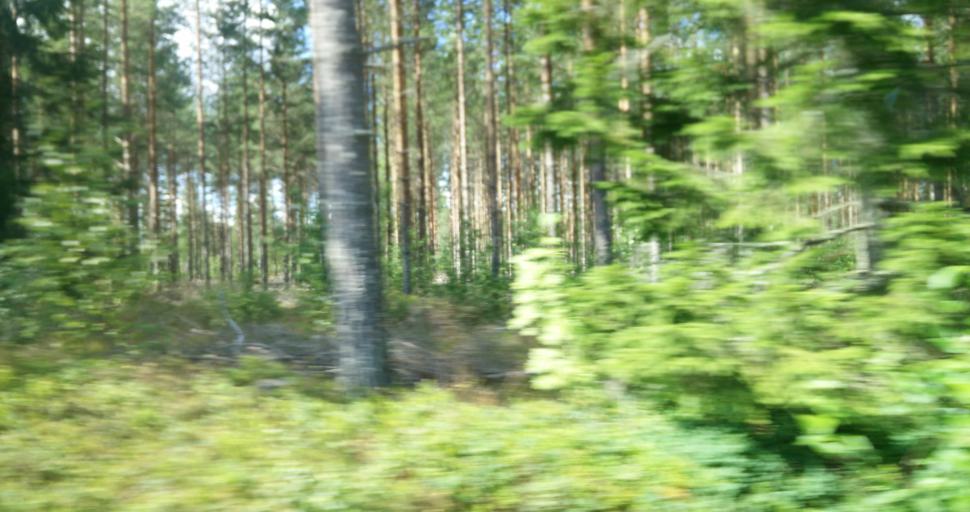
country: SE
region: Vaermland
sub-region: Hagfors Kommun
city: Hagfors
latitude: 60.0234
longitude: 13.5551
